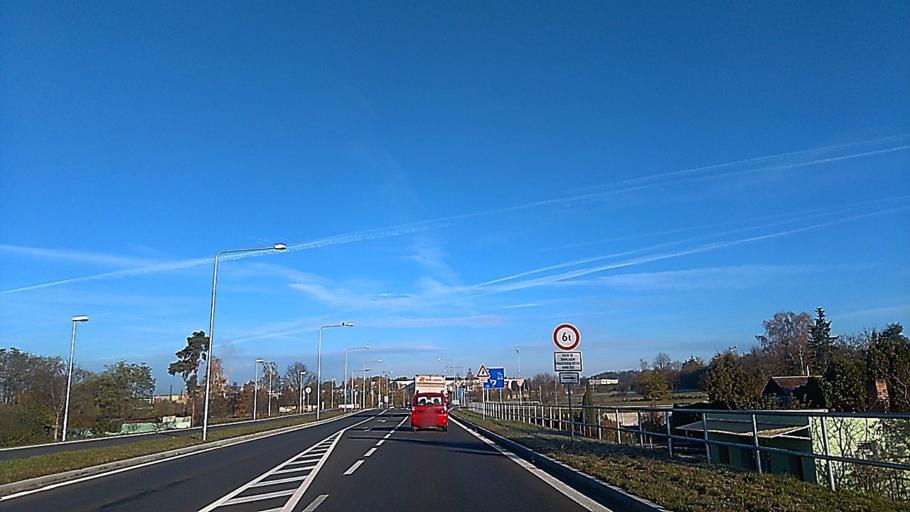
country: CZ
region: Jihocesky
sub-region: Okres Ceske Budejovice
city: Ceske Budejovice
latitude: 48.9871
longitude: 14.4844
